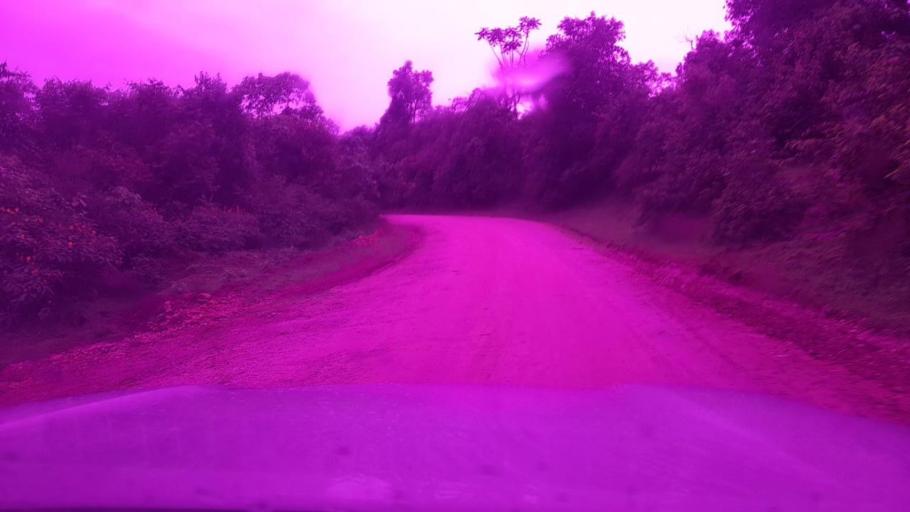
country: ET
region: Southern Nations, Nationalities, and People's Region
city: Bonga
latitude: 7.4494
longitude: 36.1335
